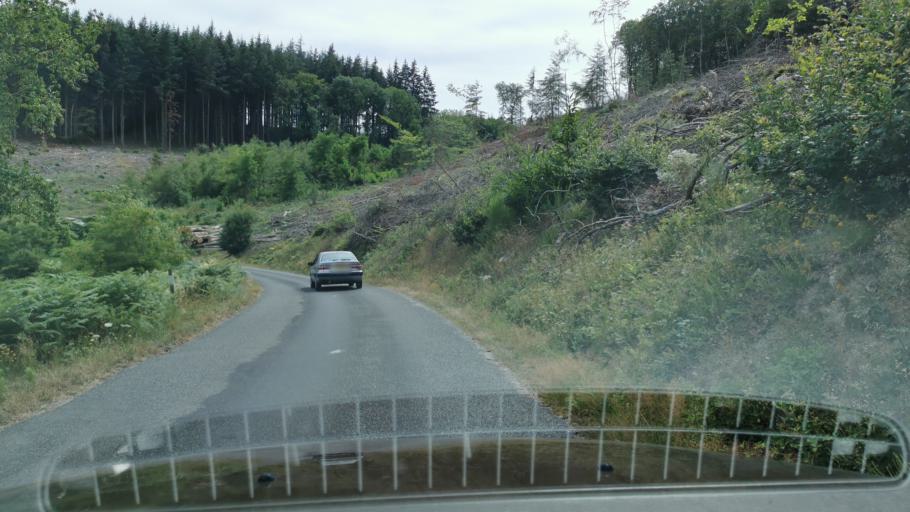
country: FR
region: Bourgogne
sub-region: Departement de Saone-et-Loire
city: Marmagne
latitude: 46.8075
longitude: 4.2880
